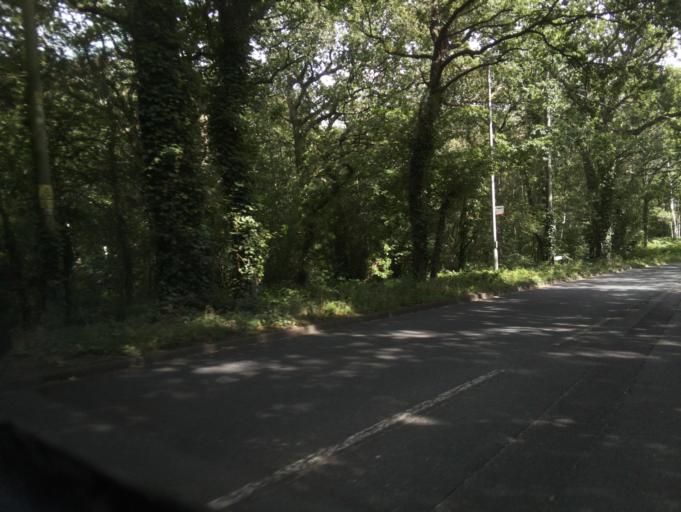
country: GB
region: England
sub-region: Hampshire
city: New Milton
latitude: 50.7468
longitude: -1.6887
